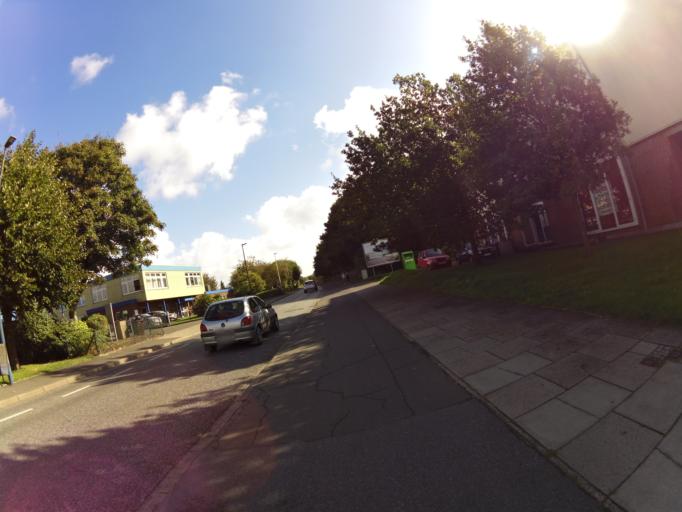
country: DE
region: Schleswig-Holstein
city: Eckernforde
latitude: 54.4495
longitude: 9.8371
